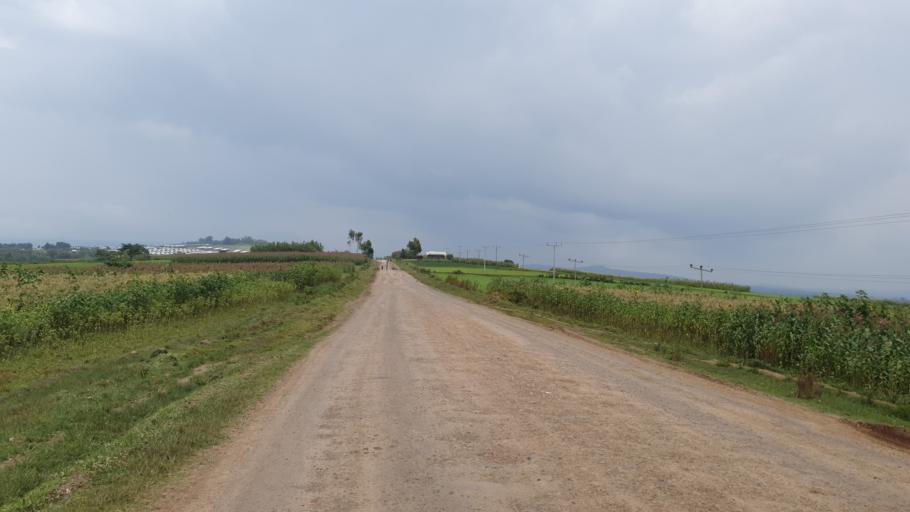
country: ET
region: Amhara
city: Bure
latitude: 10.6720
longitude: 37.0561
